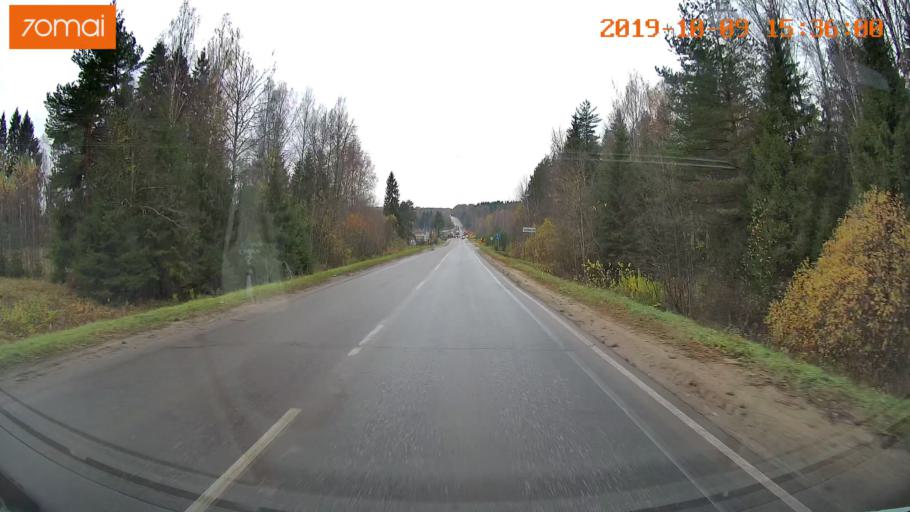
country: RU
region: Kostroma
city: Oktyabr'skiy
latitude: 57.9267
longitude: 41.2164
